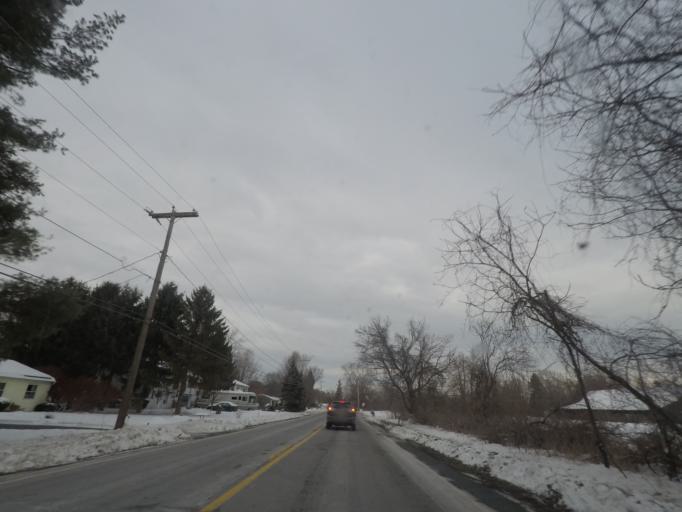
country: US
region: New York
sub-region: Greene County
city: Coxsackie
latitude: 42.3513
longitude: -73.7438
